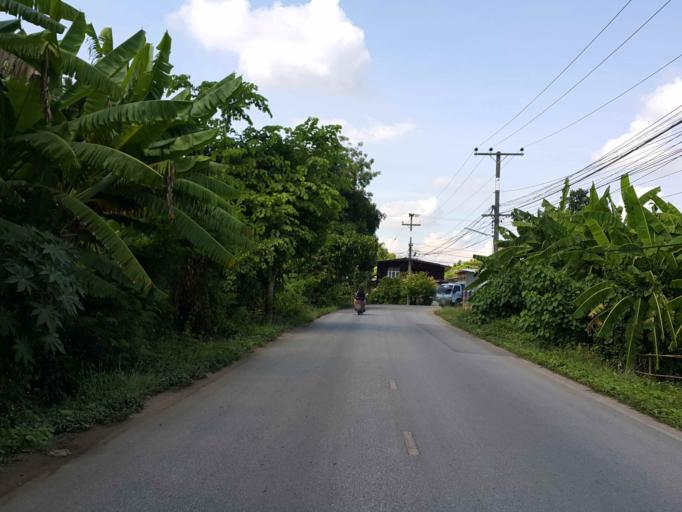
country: TH
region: Chiang Mai
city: Saraphi
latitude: 18.7180
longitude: 99.0569
